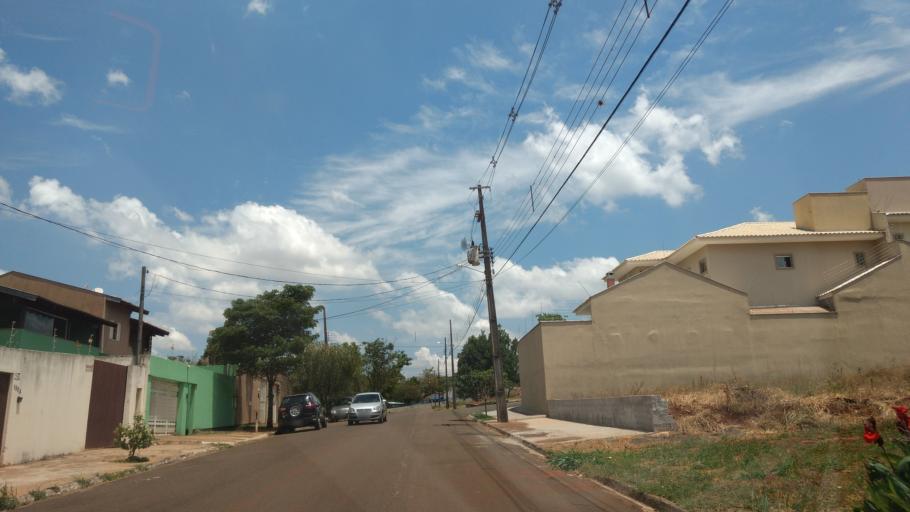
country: BR
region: Parana
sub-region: Londrina
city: Londrina
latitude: -23.3196
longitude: -51.1891
